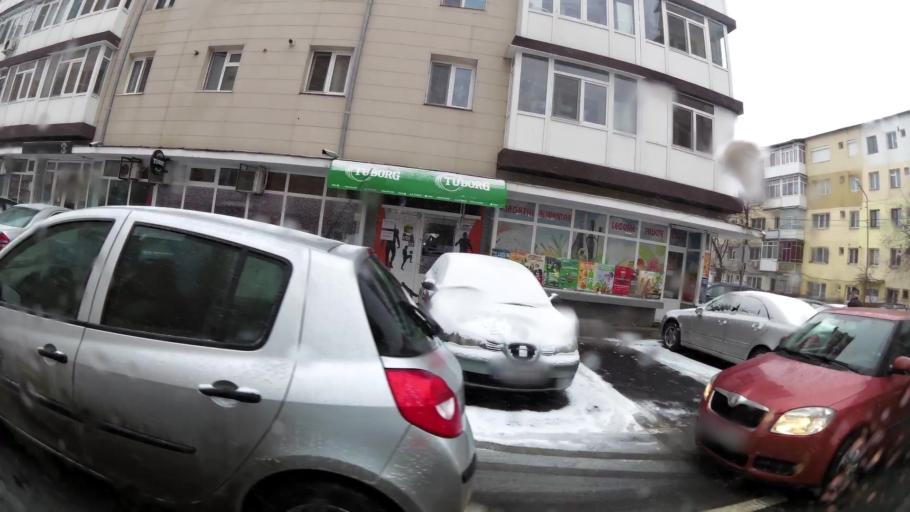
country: RO
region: Dambovita
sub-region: Municipiul Targoviste
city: Targoviste
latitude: 44.9302
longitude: 25.4491
